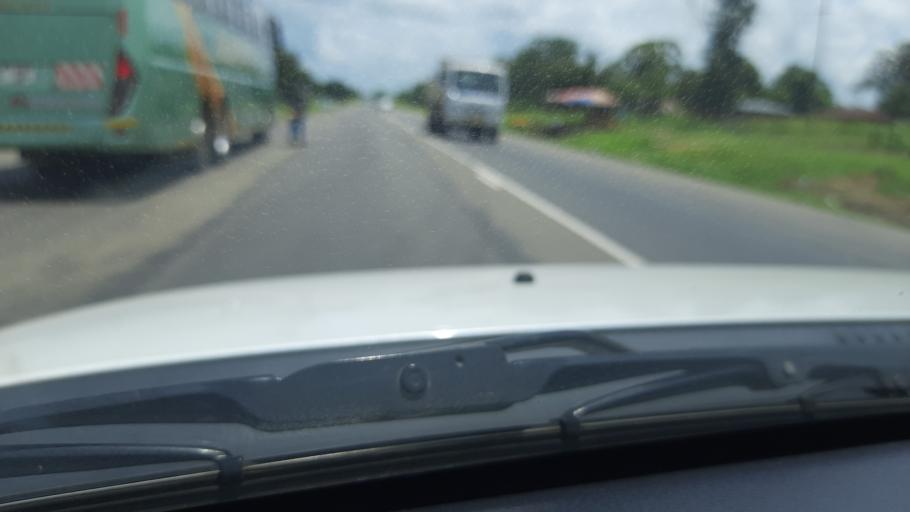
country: TZ
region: Pwani
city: Chalinze
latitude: -6.6261
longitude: 38.2697
